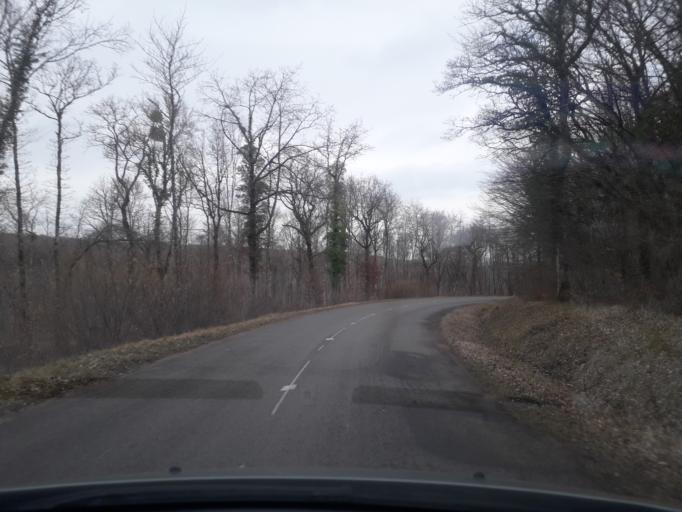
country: FR
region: Bourgogne
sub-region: Departement de la Cote-d'Or
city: Messigny-et-Vantoux
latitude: 47.4734
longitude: 4.9524
